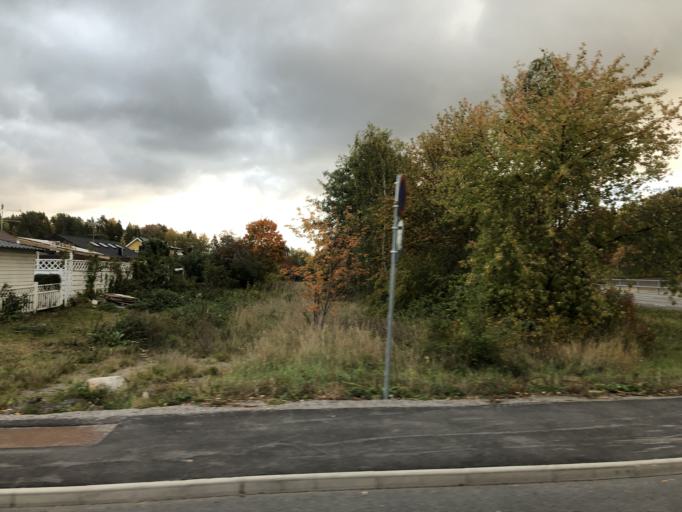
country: SE
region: Stockholm
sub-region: Jarfalla Kommun
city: Jakobsberg
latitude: 59.4225
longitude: 17.8070
